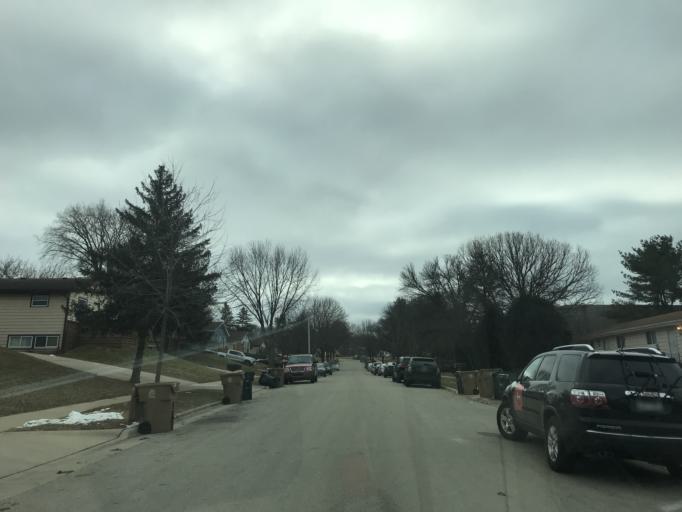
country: US
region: Wisconsin
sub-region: Dane County
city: Monona
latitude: 43.1099
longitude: -89.3072
